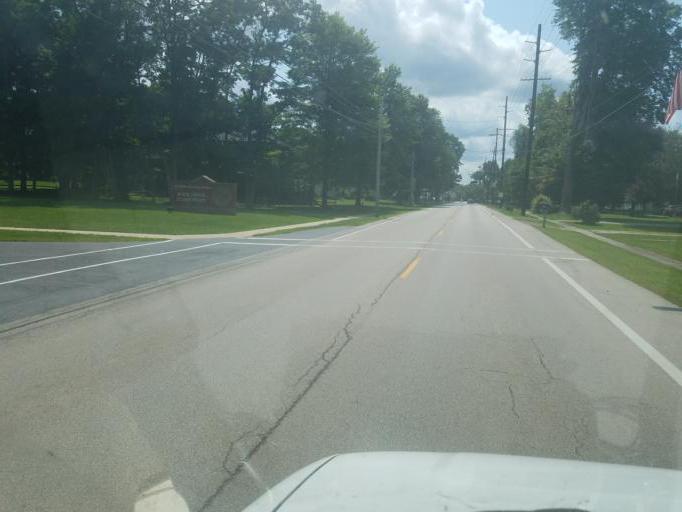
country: US
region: Ohio
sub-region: Ashtabula County
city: Roaming Shores
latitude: 41.6646
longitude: -80.8592
